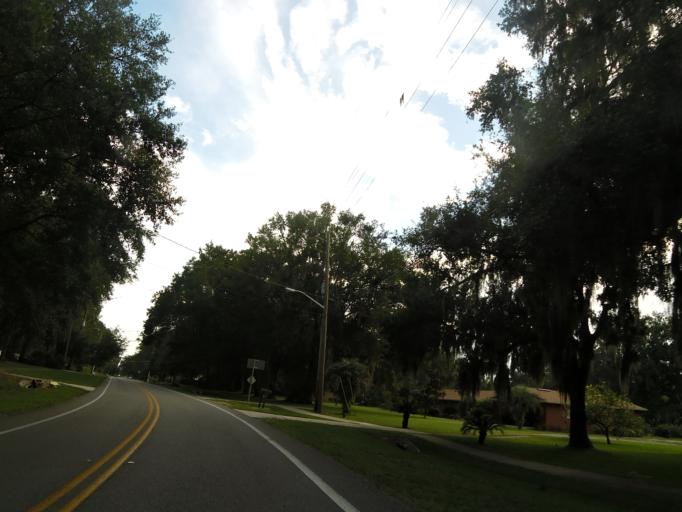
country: US
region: Florida
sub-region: Saint Johns County
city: Fruit Cove
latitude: 30.1202
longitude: -81.6360
